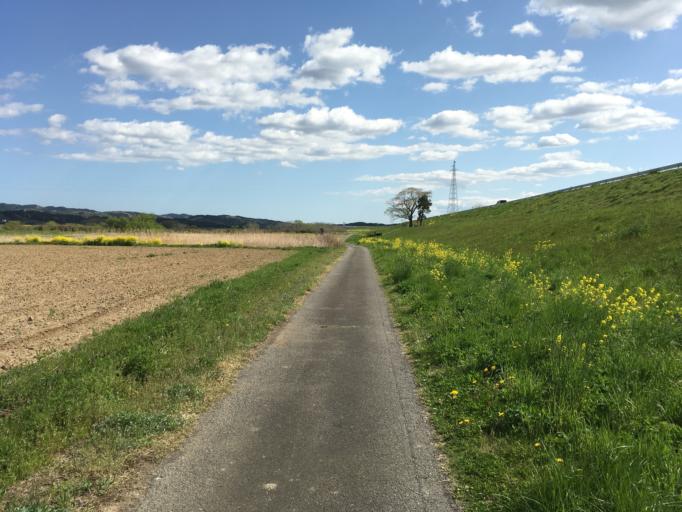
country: JP
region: Miyagi
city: Wakuya
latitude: 38.7193
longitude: 141.2645
